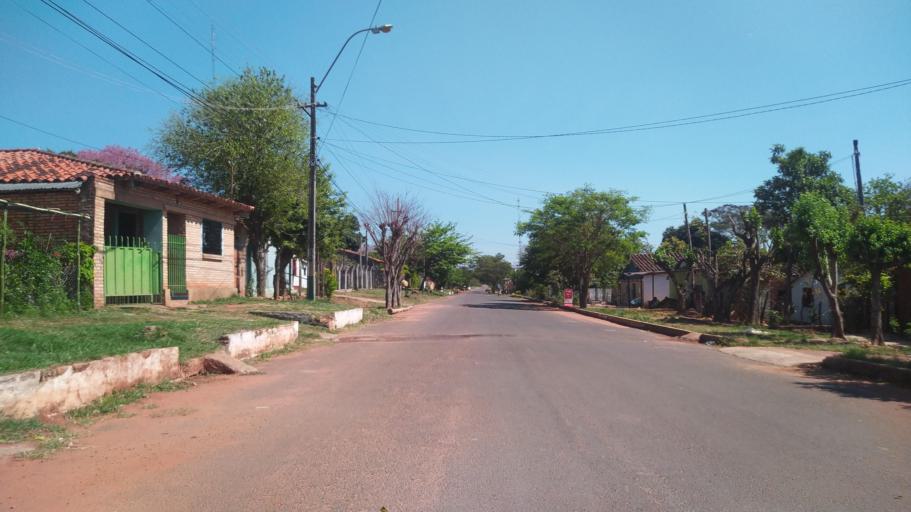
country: PY
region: Misiones
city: San Juan Bautista
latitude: -26.6644
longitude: -57.1461
